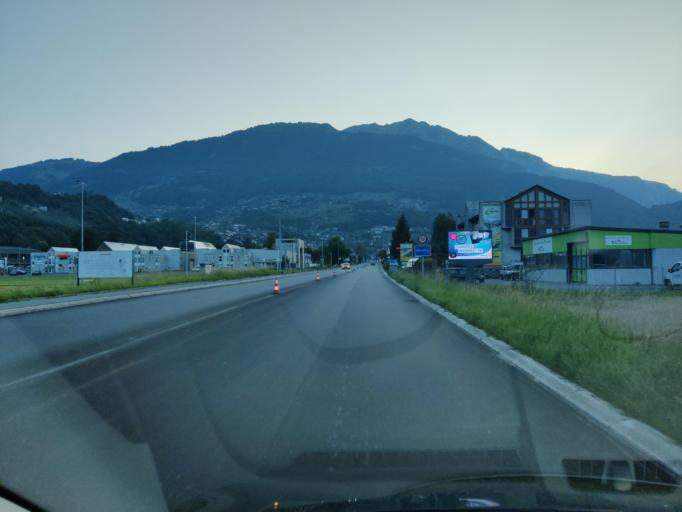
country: CH
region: Valais
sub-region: Monthey District
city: Monthey
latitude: 46.2471
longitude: 6.9633
